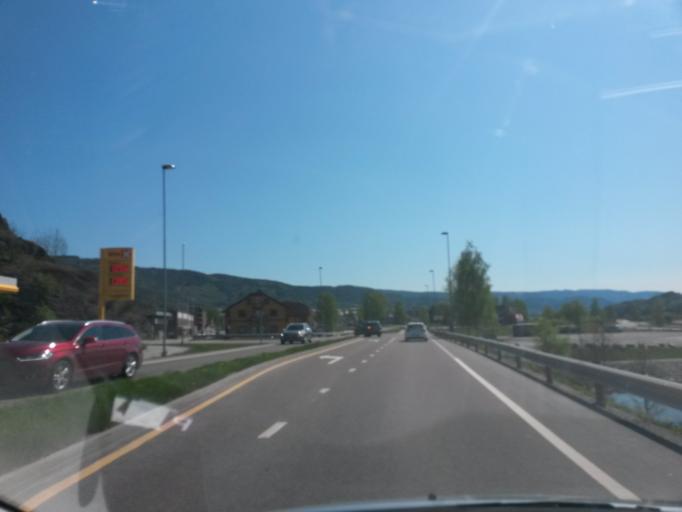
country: NO
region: Telemark
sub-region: Notodden
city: Notodden
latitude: 59.5607
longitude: 9.2473
